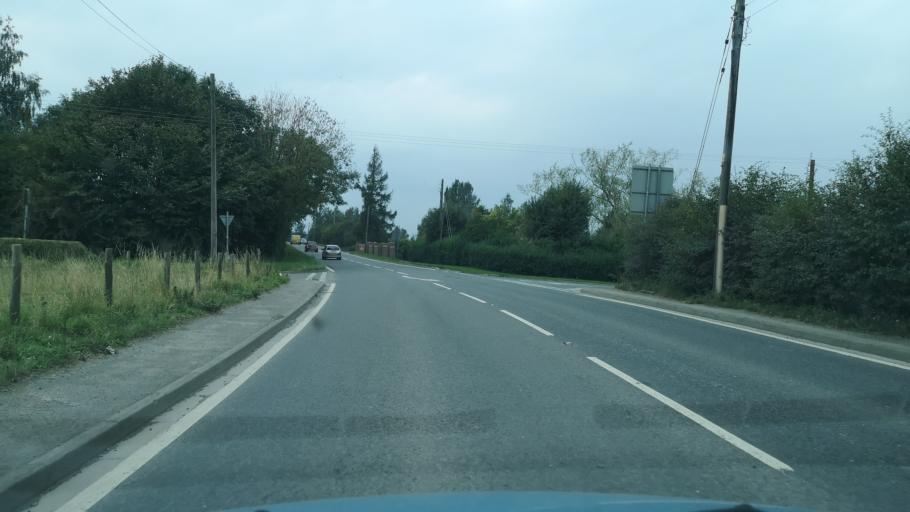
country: GB
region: England
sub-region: East Riding of Yorkshire
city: Pollington
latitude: 53.6996
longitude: -1.1247
